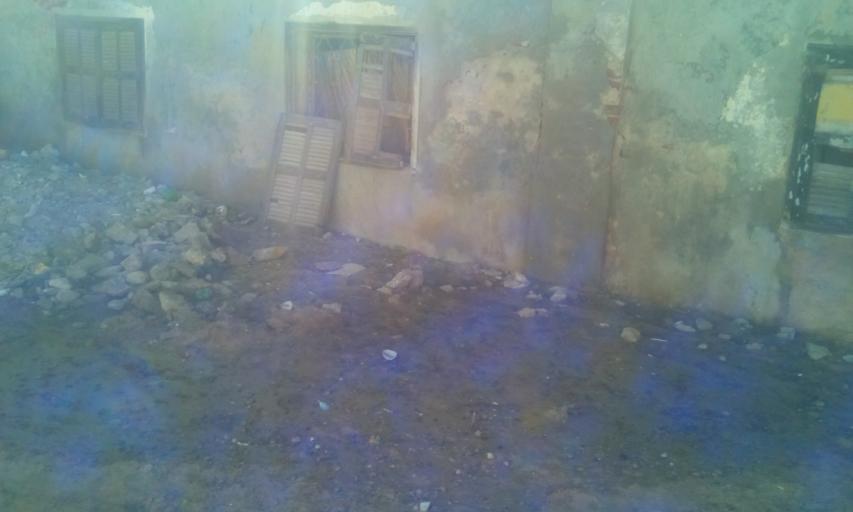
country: SN
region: Saint-Louis
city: Saint-Louis
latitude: 16.0308
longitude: -16.5083
